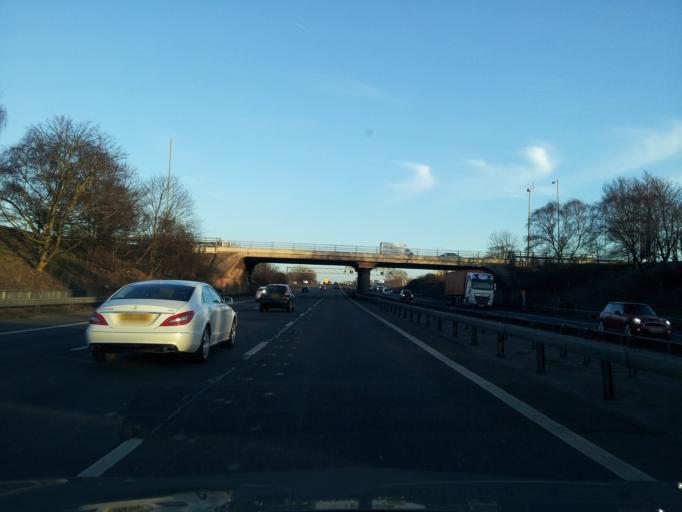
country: GB
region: England
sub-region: Central Bedfordshire
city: Husborne Crawley
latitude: 52.0269
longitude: -0.6046
